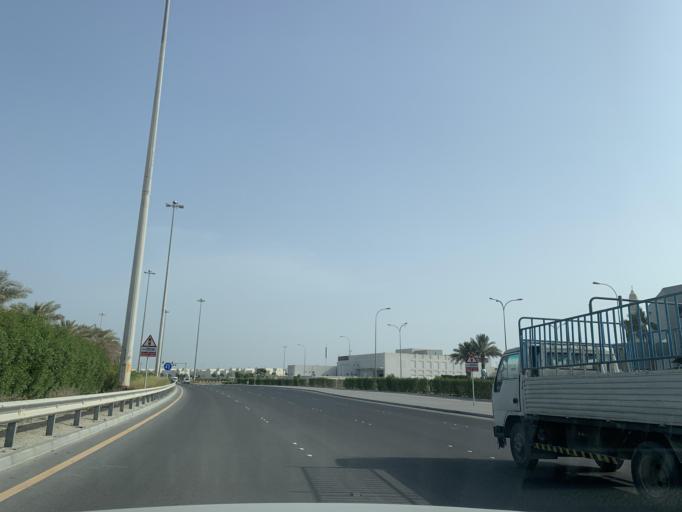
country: BH
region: Muharraq
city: Al Muharraq
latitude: 26.3073
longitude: 50.6395
